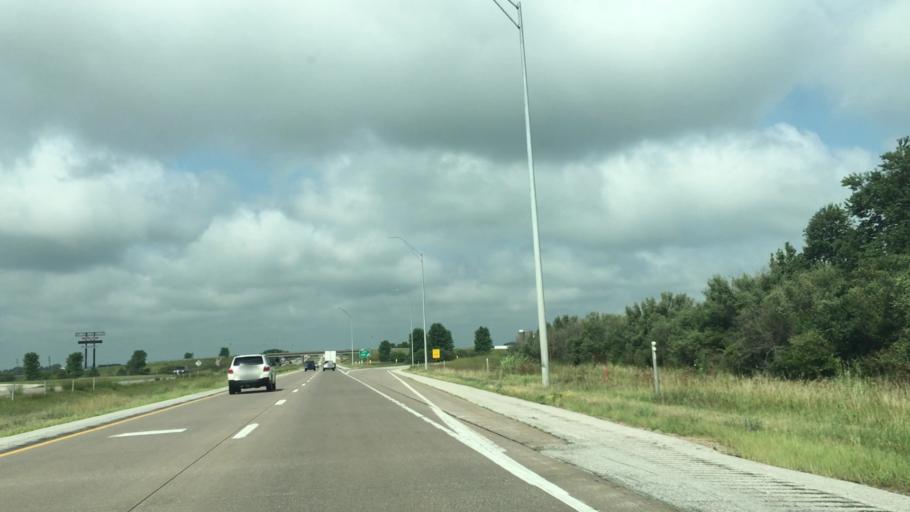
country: US
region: Iowa
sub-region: Cedar County
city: Durant
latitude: 41.6331
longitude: -90.8549
